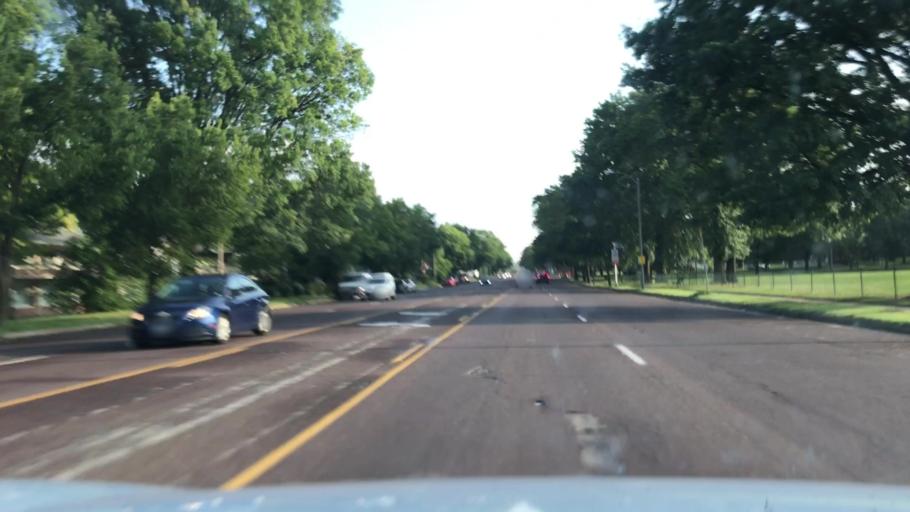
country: US
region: Missouri
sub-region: Saint Louis County
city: Maplewood
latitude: 38.5963
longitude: -90.3089
